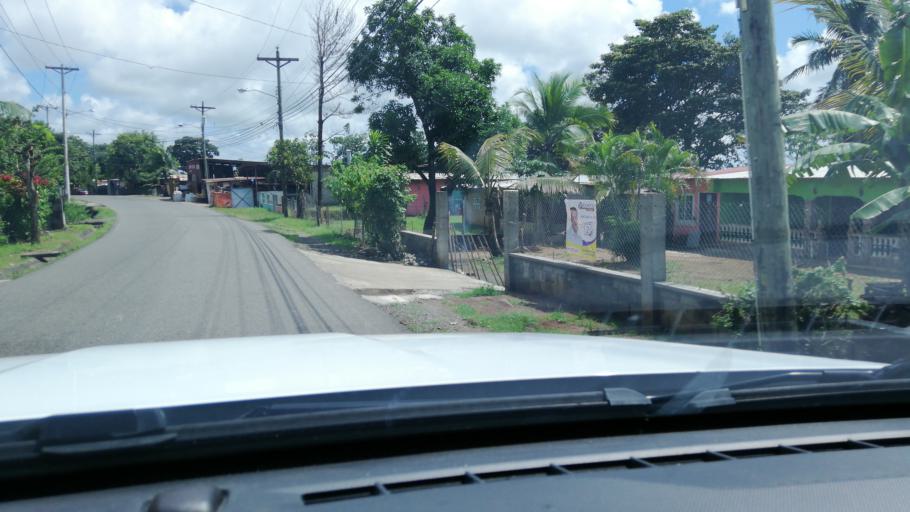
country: PA
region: Panama
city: Cabra Numero Uno
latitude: 9.1098
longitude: -79.3427
